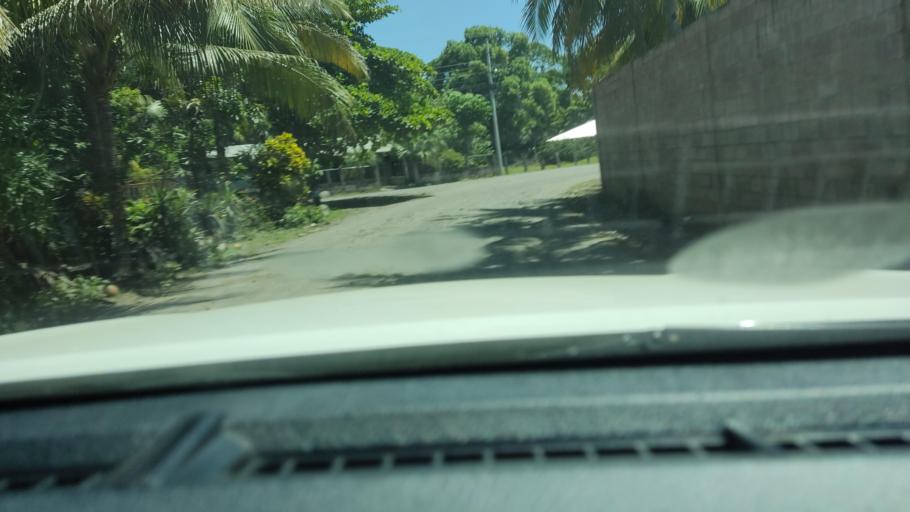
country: SV
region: Ahuachapan
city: San Francisco Menendez
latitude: 13.7512
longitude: -90.1213
